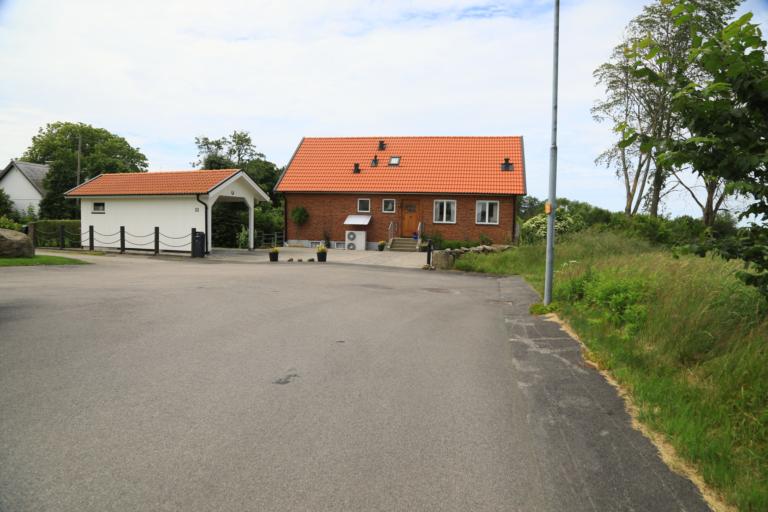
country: SE
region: Halland
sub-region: Varbergs Kommun
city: Varberg
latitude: 57.1280
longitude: 12.2675
